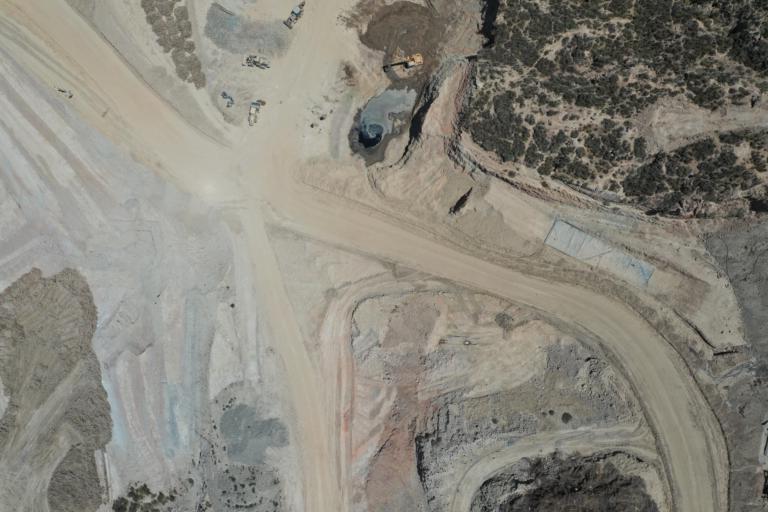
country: BO
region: La Paz
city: La Paz
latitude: -16.5568
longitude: -68.1290
